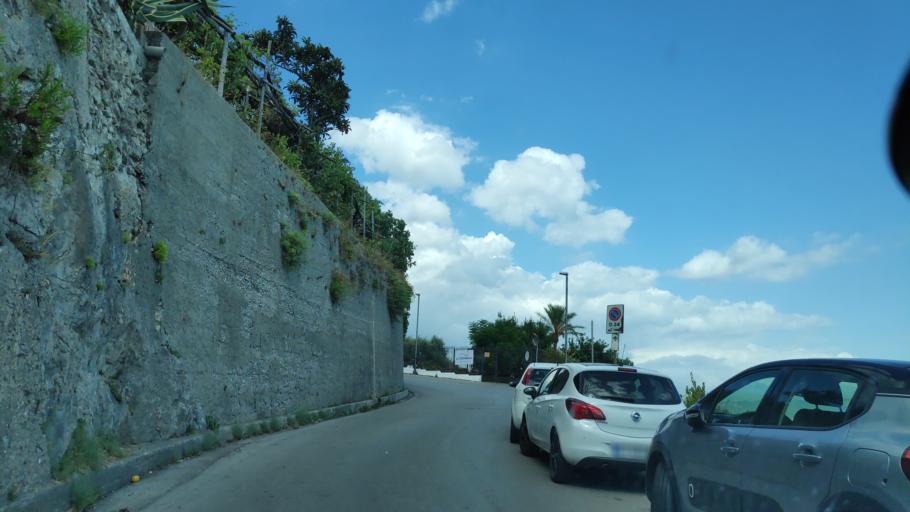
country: IT
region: Campania
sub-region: Provincia di Salerno
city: Vietri sul Mare
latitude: 40.6693
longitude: 14.7308
